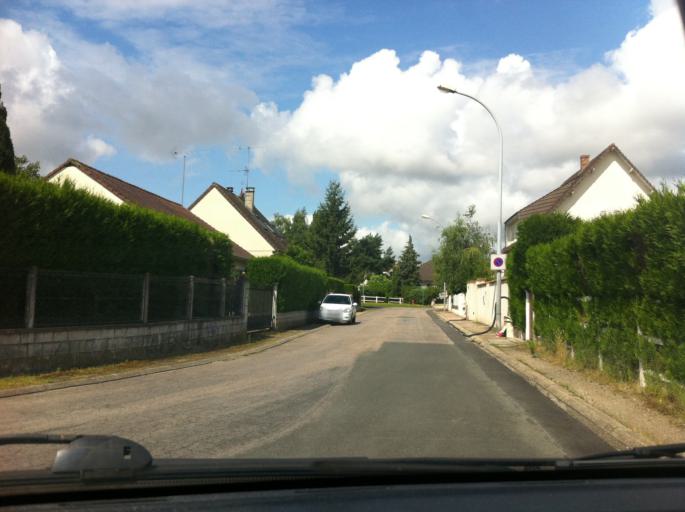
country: FR
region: Ile-de-France
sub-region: Departement de l'Essonne
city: Etrechy
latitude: 48.4857
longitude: 2.1859
